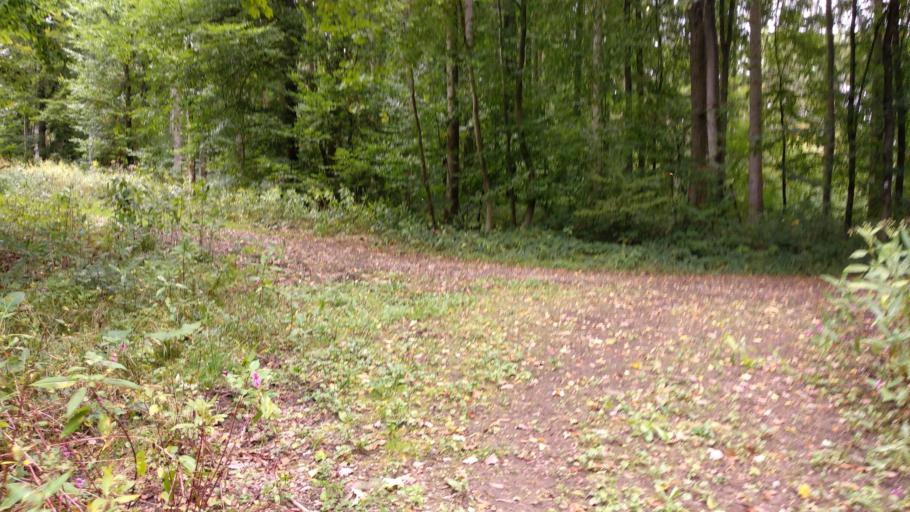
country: DE
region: North Rhine-Westphalia
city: Beverungen
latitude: 51.6895
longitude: 9.3713
